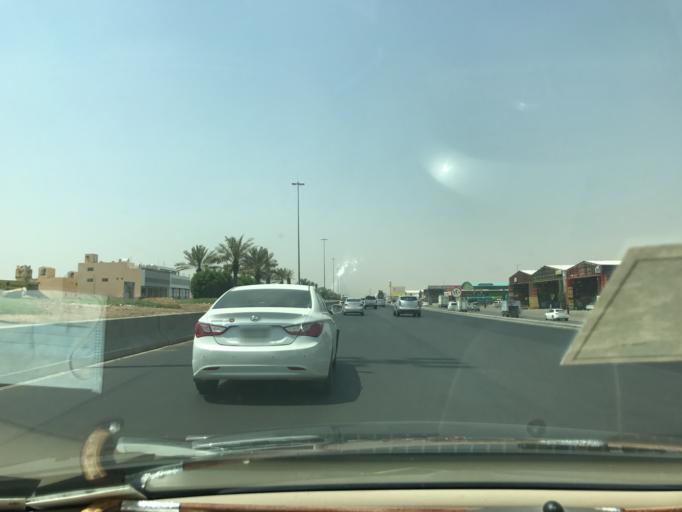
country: SA
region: Ar Riyad
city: Riyadh
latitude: 24.8209
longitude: 46.7891
